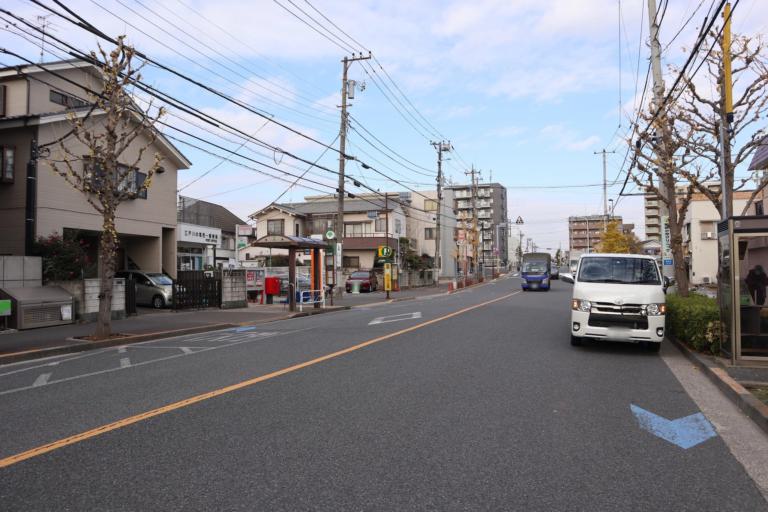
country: JP
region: Tokyo
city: Urayasu
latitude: 35.6733
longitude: 139.8720
